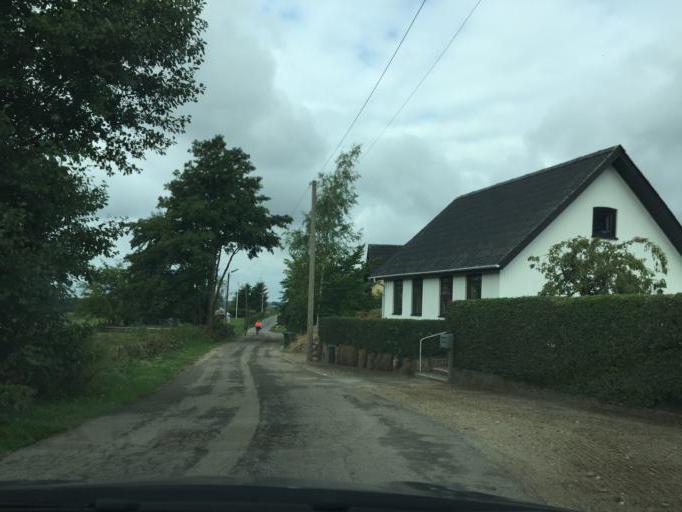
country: DK
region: South Denmark
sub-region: Assens Kommune
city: Harby
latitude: 55.1977
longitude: 10.1507
